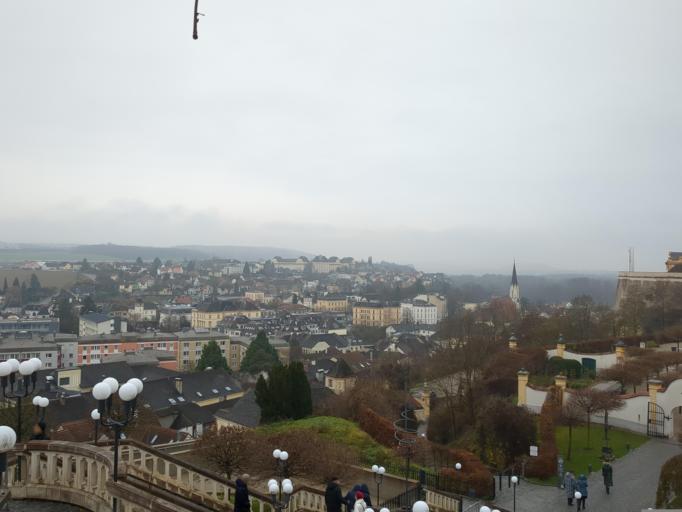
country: AT
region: Lower Austria
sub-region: Politischer Bezirk Melk
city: Melk
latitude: 48.2283
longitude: 15.3360
